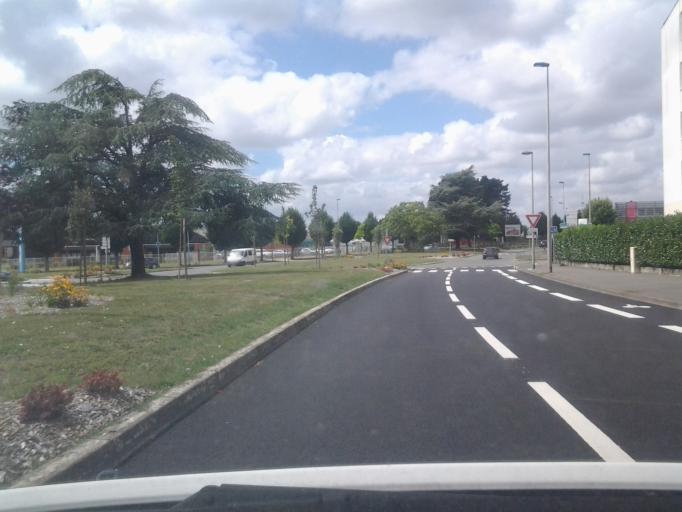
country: FR
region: Pays de la Loire
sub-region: Departement de la Vendee
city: La Roche-sur-Yon
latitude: 46.6596
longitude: -1.4397
